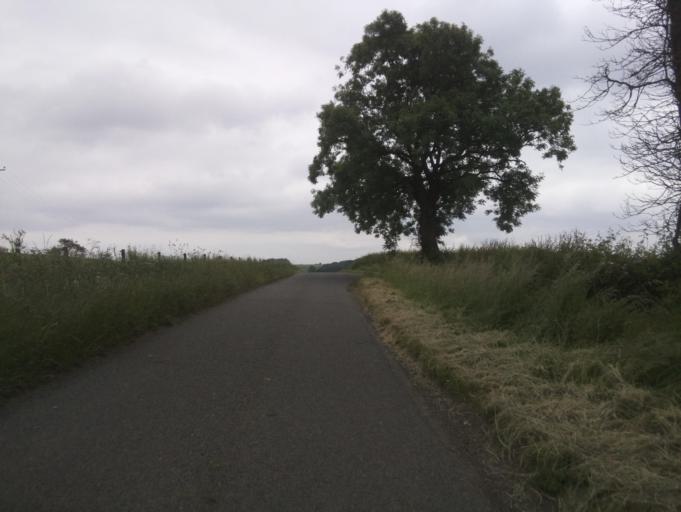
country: GB
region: England
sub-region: District of Rutland
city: Langham
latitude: 52.6786
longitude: -0.7955
